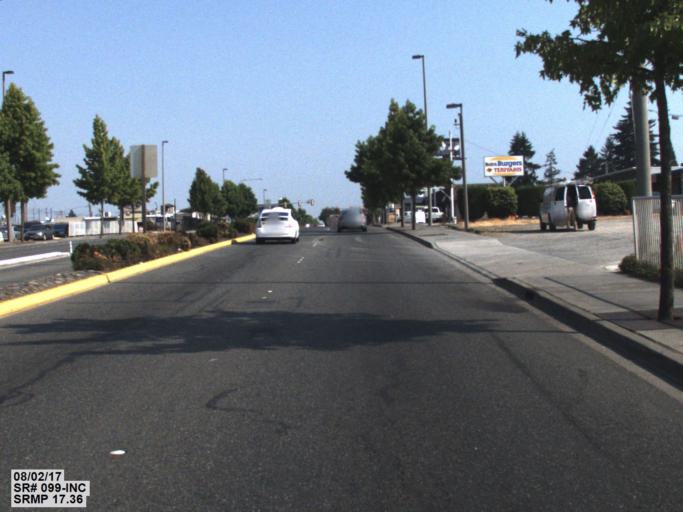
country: US
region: Washington
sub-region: King County
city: SeaTac
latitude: 47.4204
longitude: -122.2966
